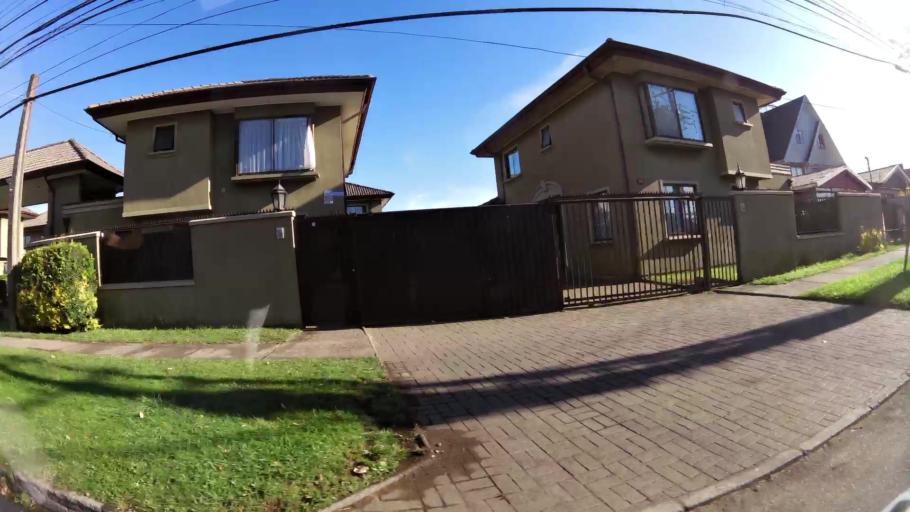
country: CL
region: Biobio
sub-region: Provincia de Concepcion
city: Concepcion
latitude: -36.8324
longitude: -73.1065
